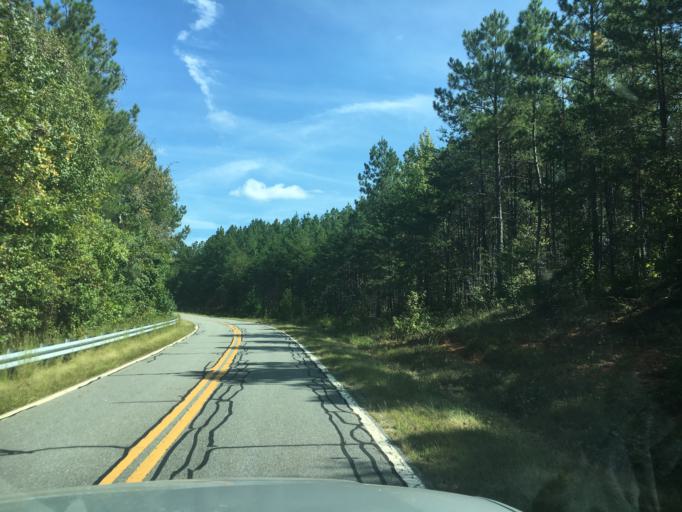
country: US
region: North Carolina
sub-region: Rutherford County
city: Forest City
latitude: 35.2309
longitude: -81.9289
